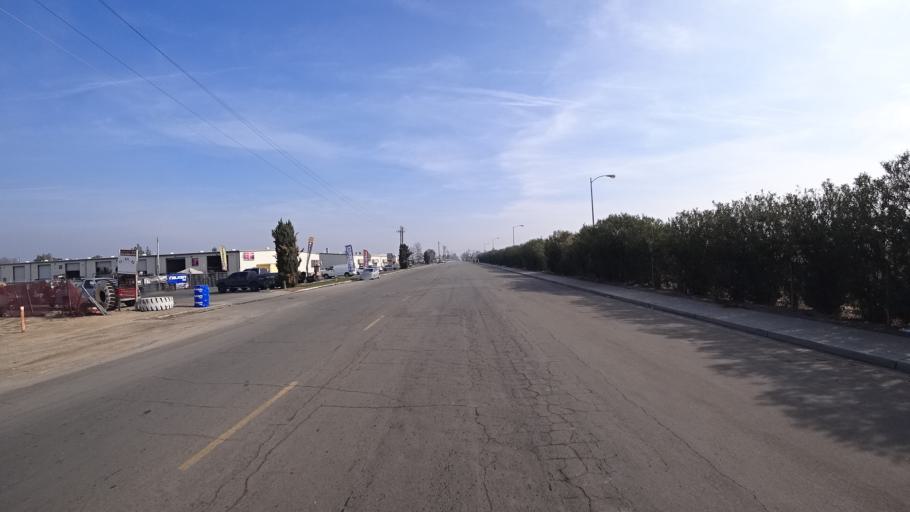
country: US
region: California
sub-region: Kern County
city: Bakersfield
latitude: 35.3467
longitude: -119.0100
